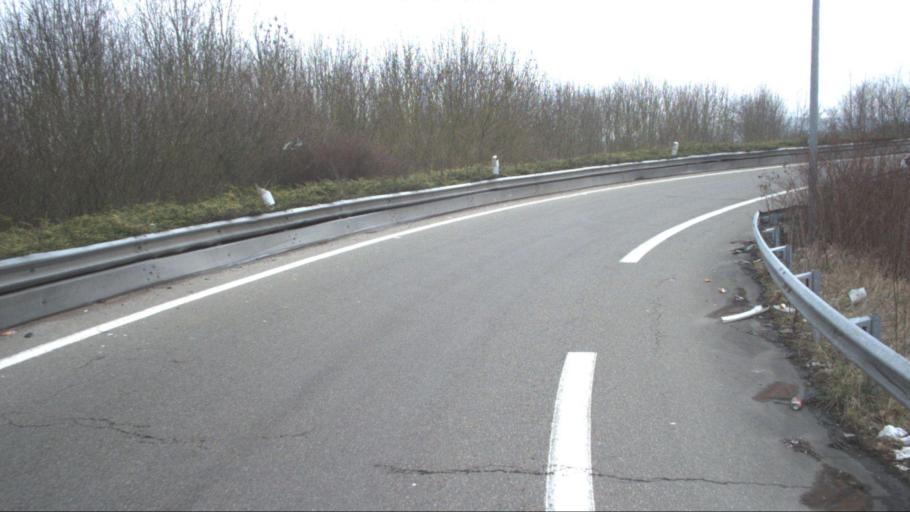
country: FR
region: Ile-de-France
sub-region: Departement des Yvelines
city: Villennes-sur-Seine
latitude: 48.9188
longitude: 2.0086
